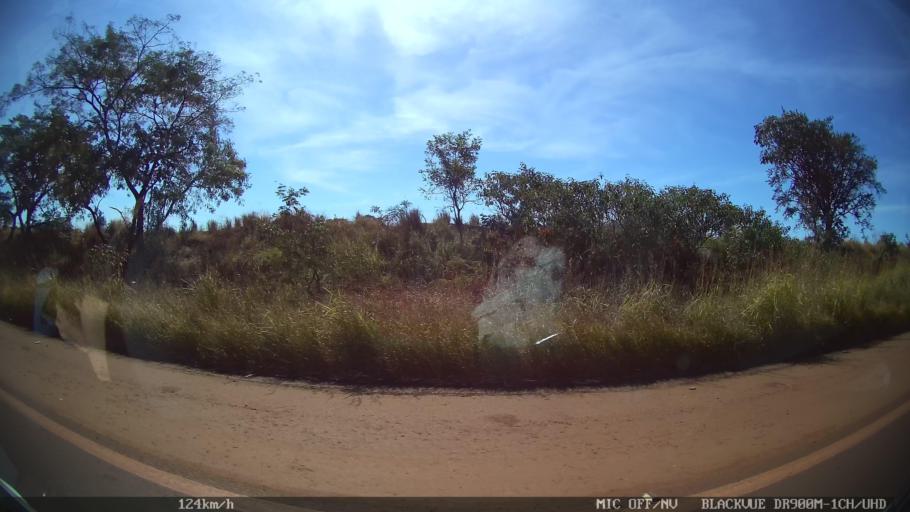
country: BR
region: Sao Paulo
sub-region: Sao Joaquim Da Barra
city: Sao Joaquim da Barra
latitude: -20.5550
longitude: -47.7191
